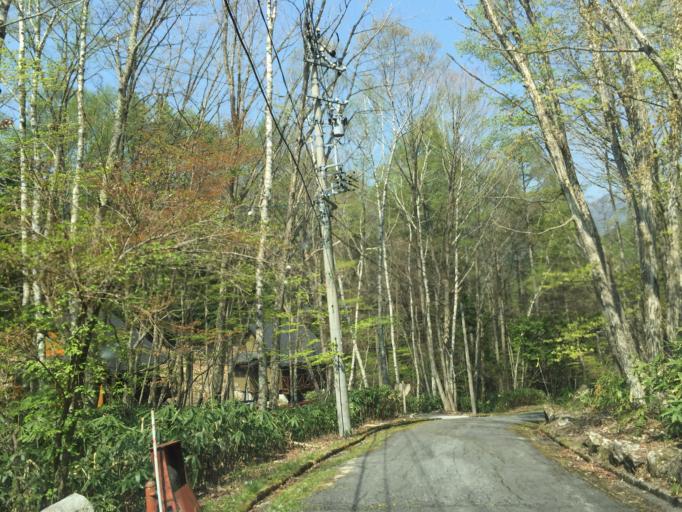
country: JP
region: Nagano
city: Iida
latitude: 35.3554
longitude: 137.6790
